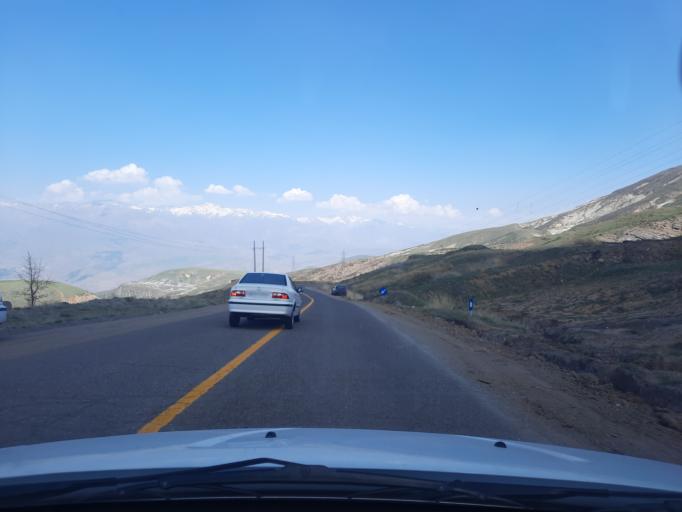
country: IR
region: Qazvin
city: Qazvin
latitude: 36.3981
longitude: 50.2153
